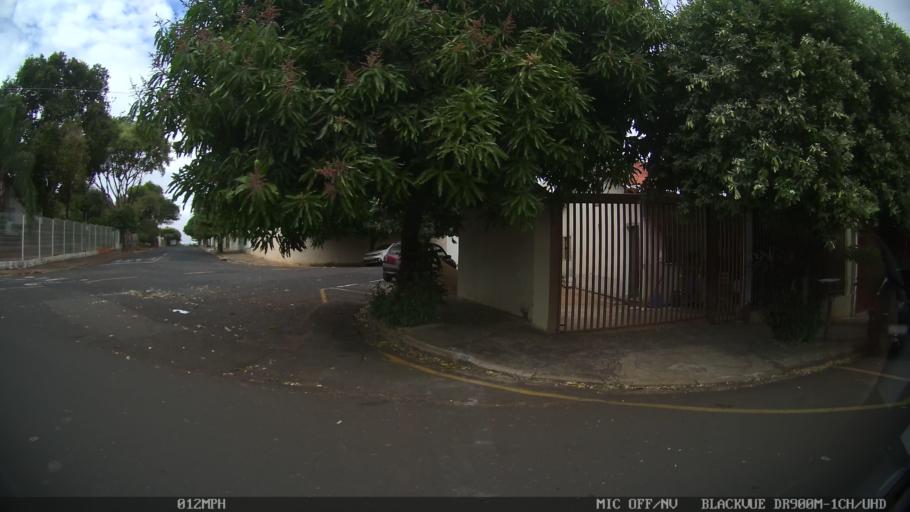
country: BR
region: Sao Paulo
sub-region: Sao Jose Do Rio Preto
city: Sao Jose do Rio Preto
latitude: -20.8149
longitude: -49.3643
